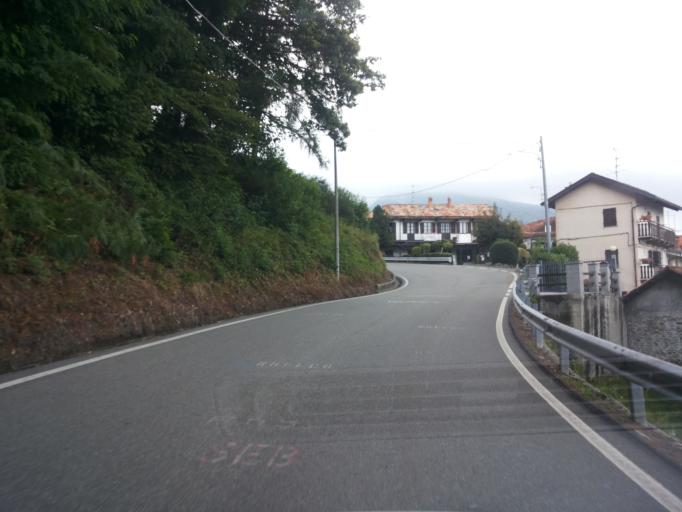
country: IT
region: Piedmont
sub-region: Provincia di Biella
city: Pollone
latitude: 45.6019
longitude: 7.9980
